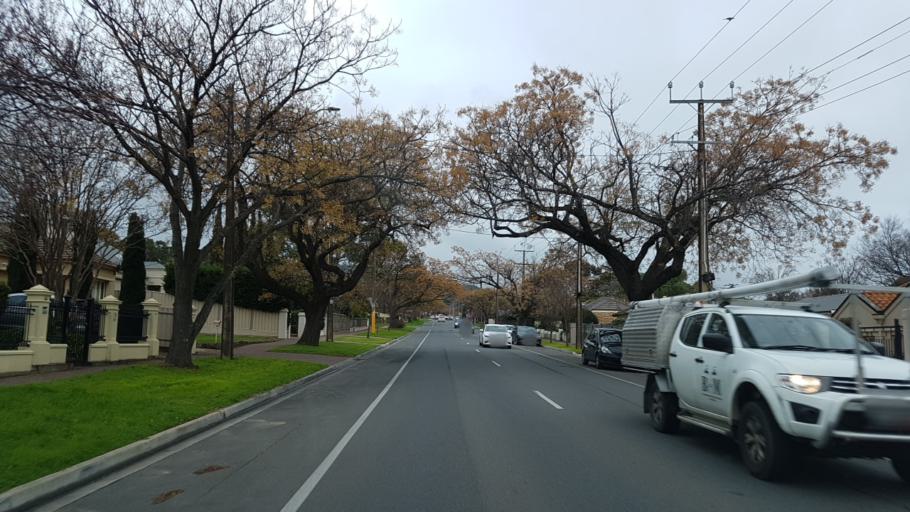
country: AU
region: South Australia
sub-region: Burnside
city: Tusmore
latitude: -34.9428
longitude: 138.6517
